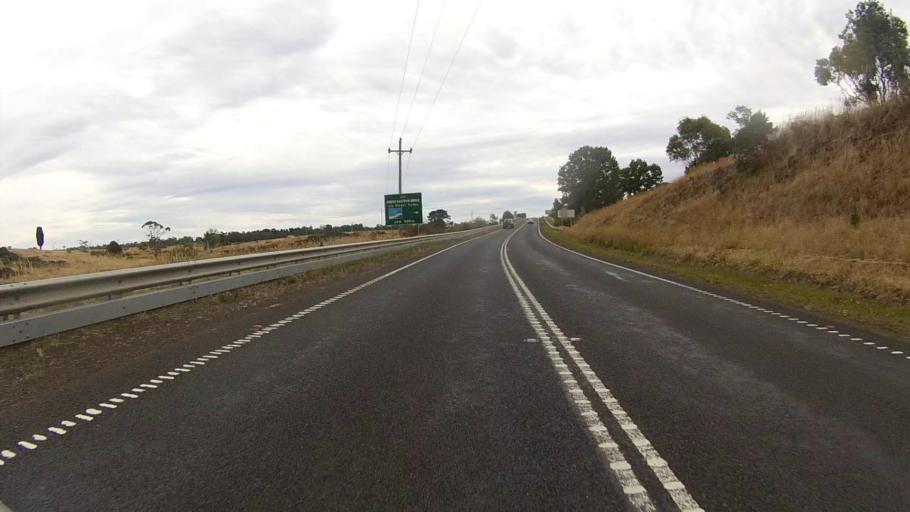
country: AU
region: Tasmania
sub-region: Northern Midlands
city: Evandale
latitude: -41.8439
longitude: 147.4482
